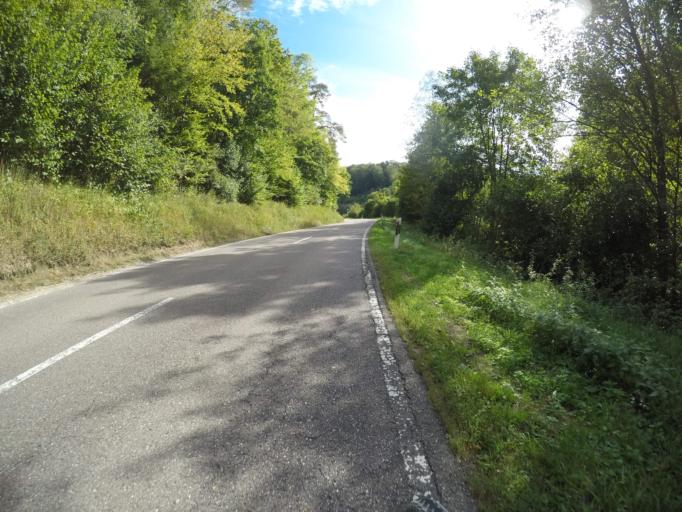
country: DE
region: Baden-Wuerttemberg
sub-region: Regierungsbezirk Stuttgart
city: Weissach
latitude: 48.8503
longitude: 8.9605
